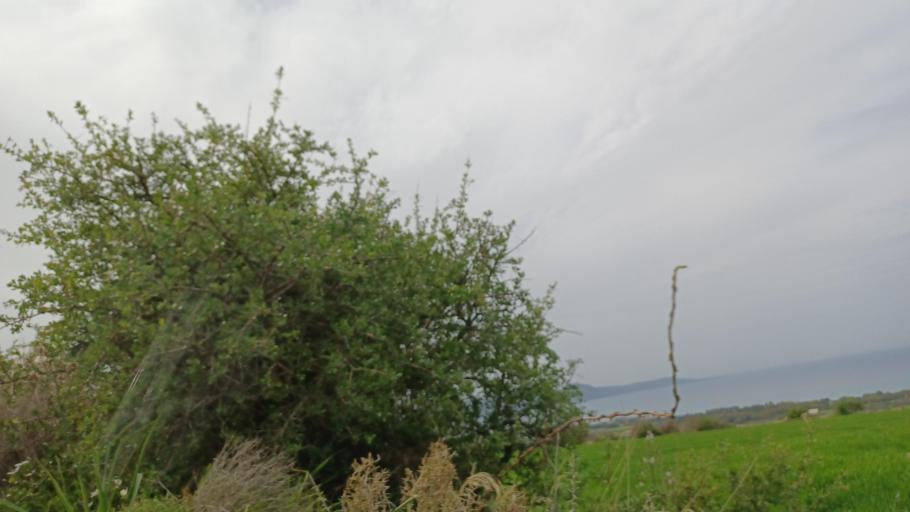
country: CY
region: Pafos
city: Polis
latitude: 35.0443
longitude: 32.4760
